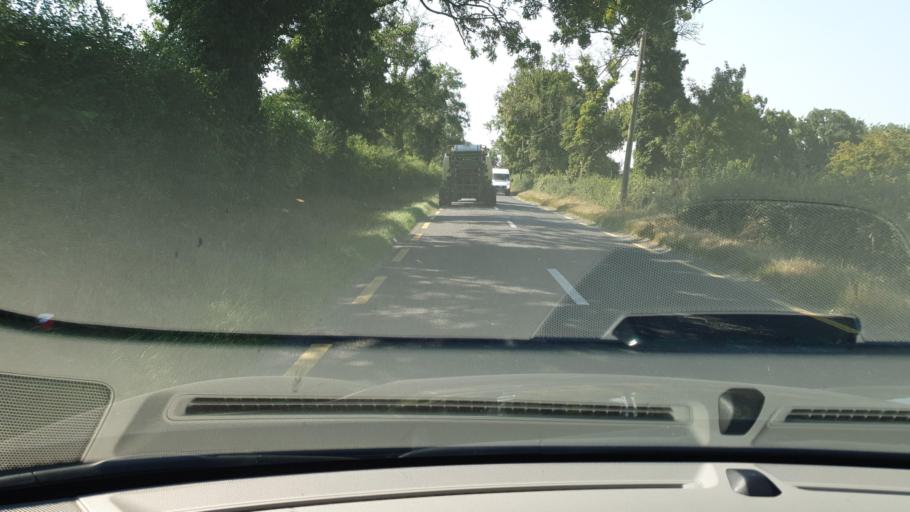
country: IE
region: Leinster
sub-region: An Mhi
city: Trim
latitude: 53.5819
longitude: -6.8482
